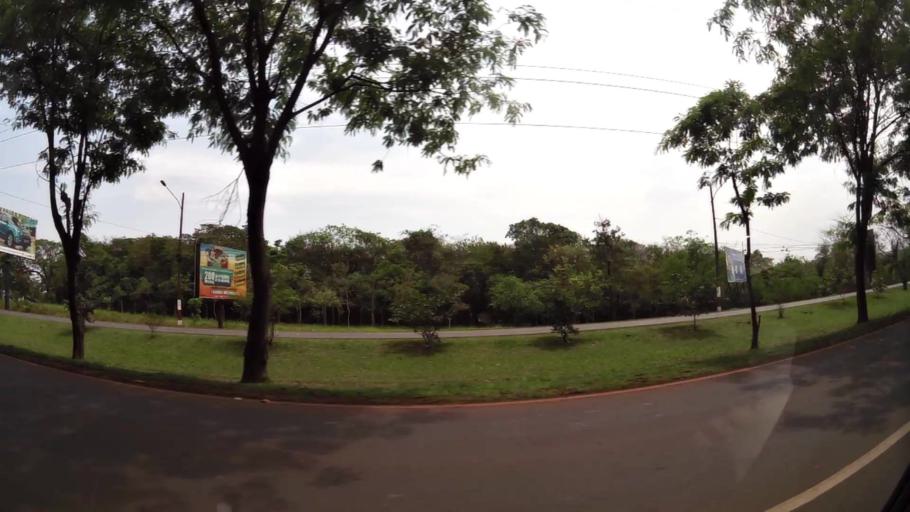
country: PY
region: Alto Parana
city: Ciudad del Este
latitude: -25.4788
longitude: -54.6256
